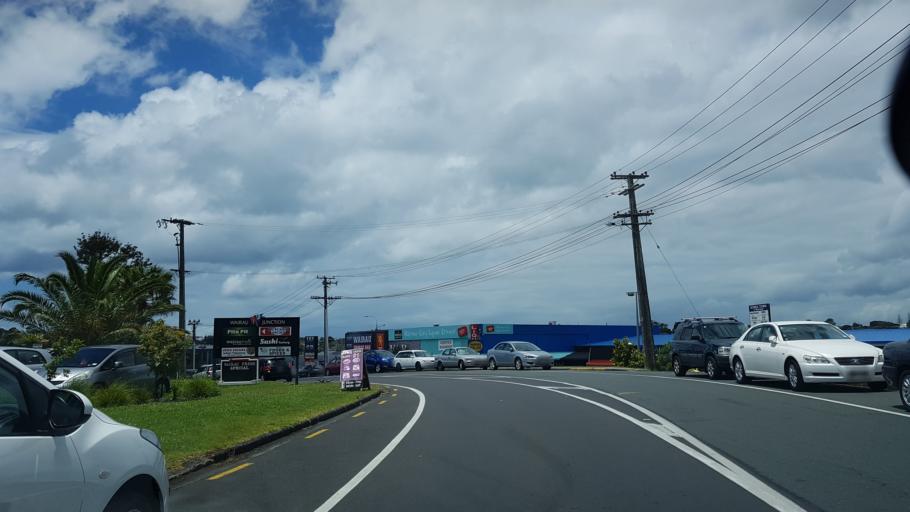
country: NZ
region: Auckland
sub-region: Auckland
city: North Shore
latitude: -36.7713
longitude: 174.7365
